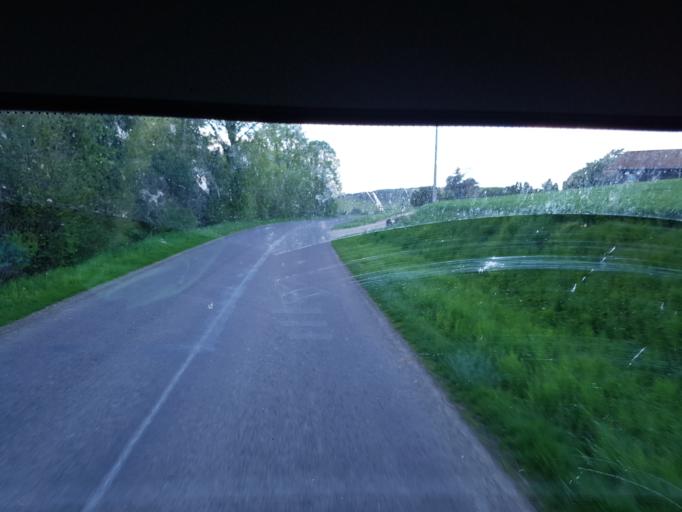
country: FR
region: Champagne-Ardenne
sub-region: Departement de l'Aube
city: Aix-en-Othe
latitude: 48.3031
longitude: 3.6374
